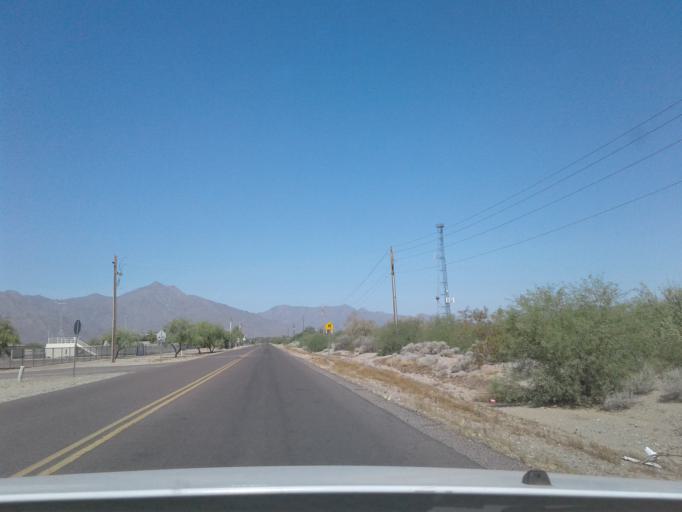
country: US
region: Arizona
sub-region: Maricopa County
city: Laveen
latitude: 33.2905
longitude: -112.1581
